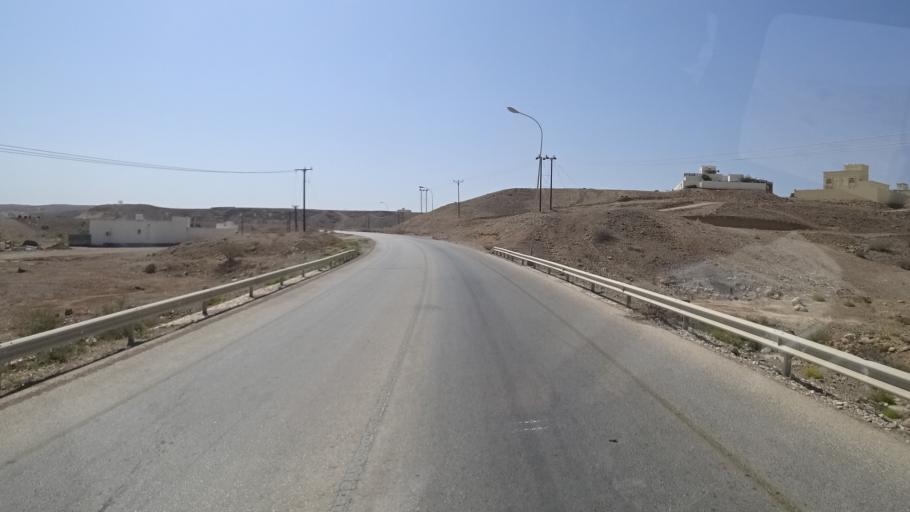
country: OM
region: Ash Sharqiyah
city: Sur
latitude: 22.5436
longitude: 59.5021
